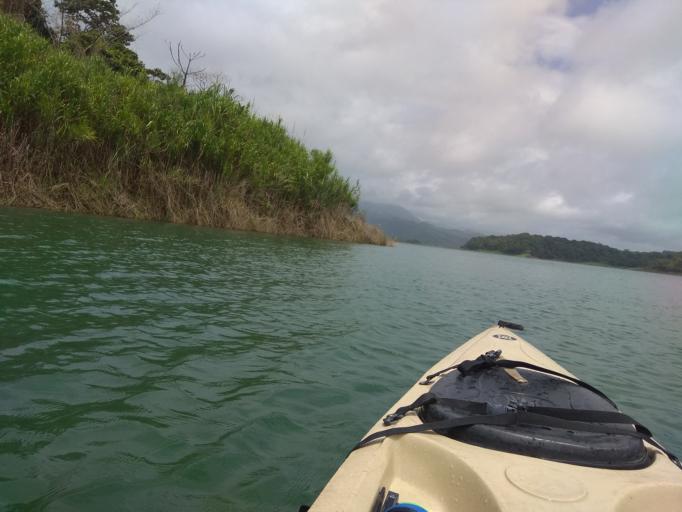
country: CR
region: Alajuela
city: La Fortuna
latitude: 10.4692
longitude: -84.7620
